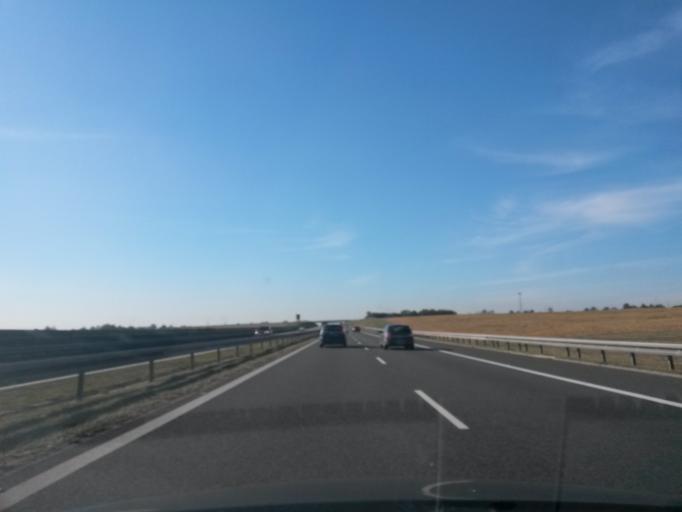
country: PL
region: Opole Voivodeship
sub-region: Powiat krapkowicki
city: Gogolin
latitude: 50.4798
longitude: 18.0624
